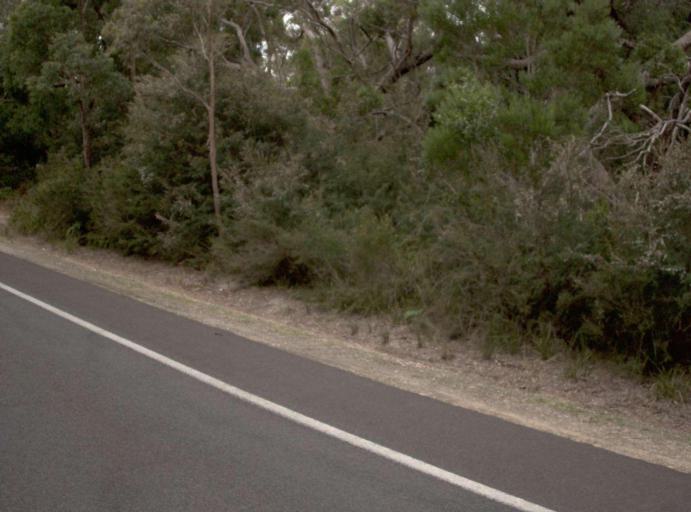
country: AU
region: Victoria
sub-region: Wellington
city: Sale
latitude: -38.1913
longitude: 147.0794
